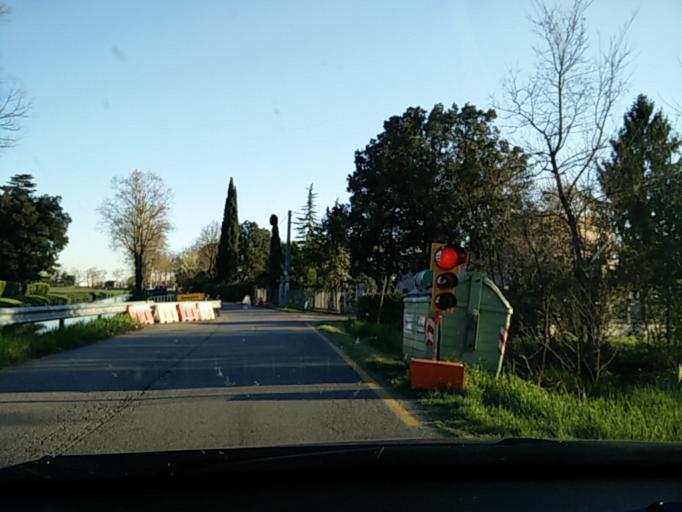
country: IT
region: Veneto
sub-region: Provincia di Venezia
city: Meolo
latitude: 45.6006
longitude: 12.4692
